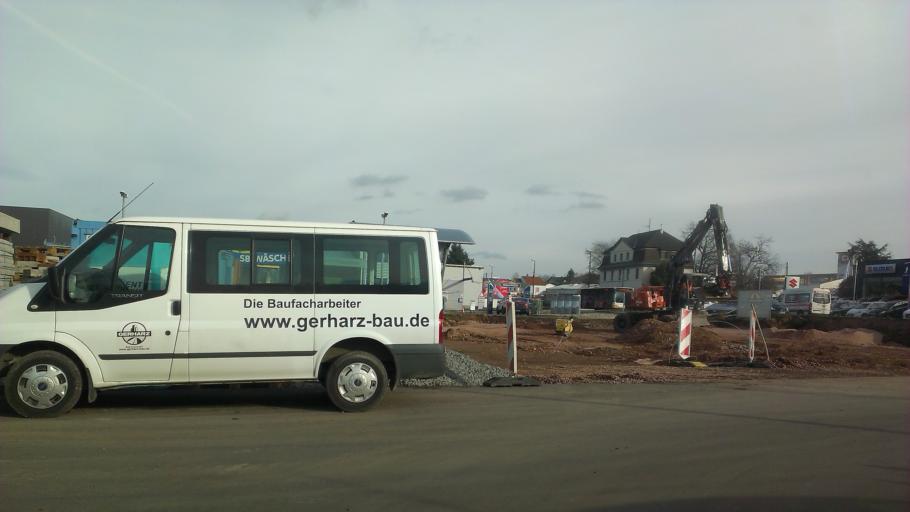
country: DE
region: Rheinland-Pfalz
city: Bretzenheim
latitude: 49.8484
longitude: 7.8890
